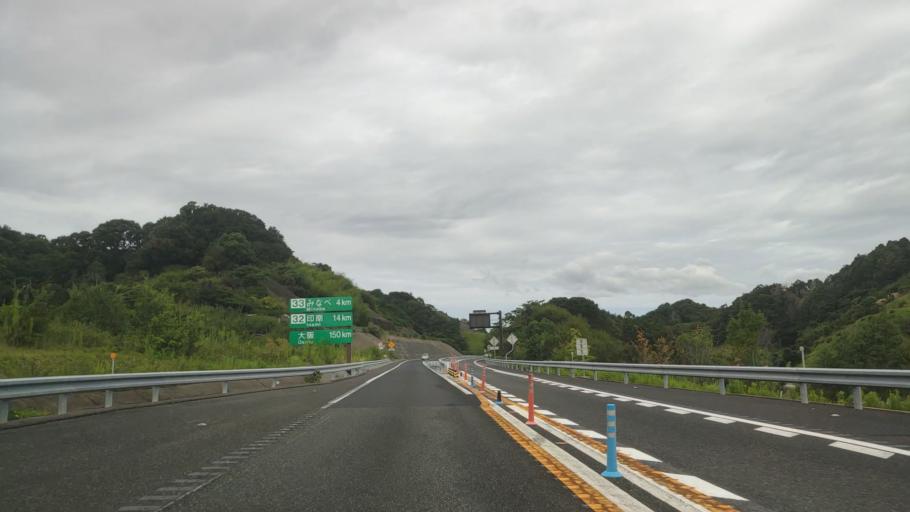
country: JP
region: Wakayama
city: Tanabe
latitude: 33.7573
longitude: 135.3546
